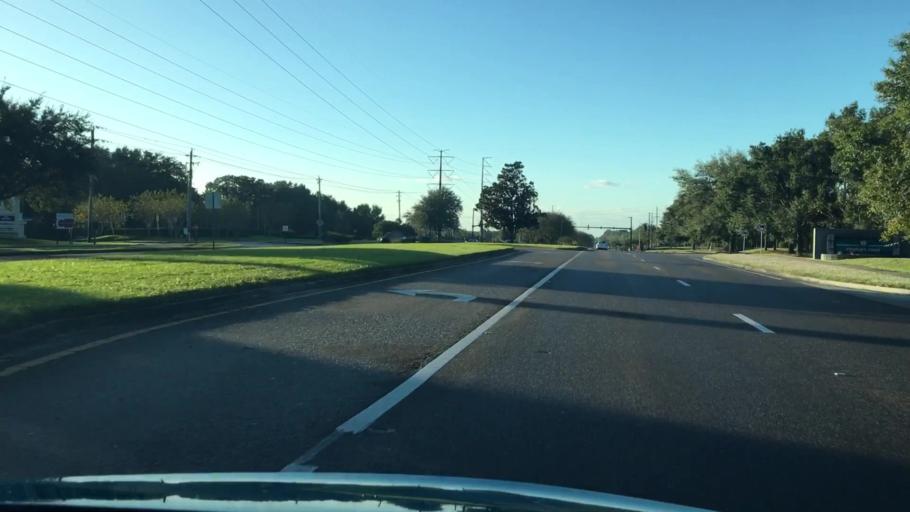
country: US
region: Florida
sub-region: Seminole County
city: Heathrow
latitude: 28.7813
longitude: -81.3474
